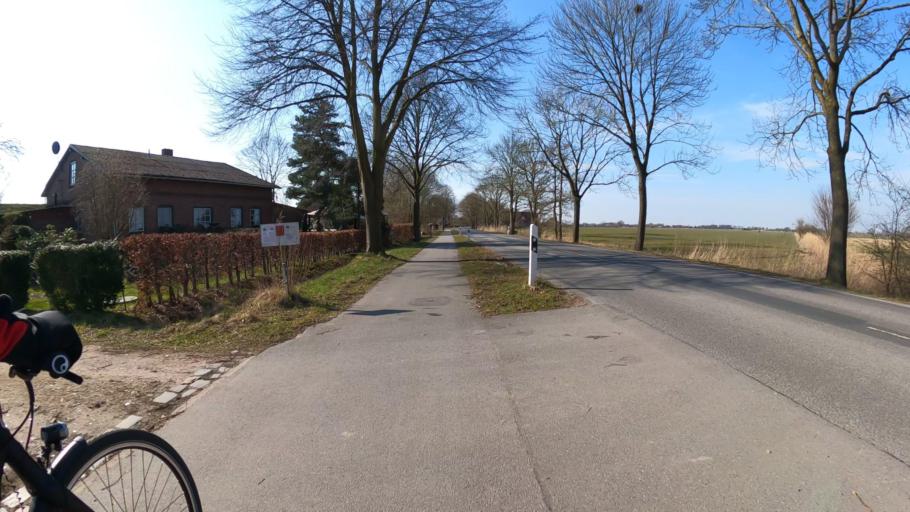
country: DE
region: Schleswig-Holstein
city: Neuendeich
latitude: 53.6754
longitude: 9.5996
